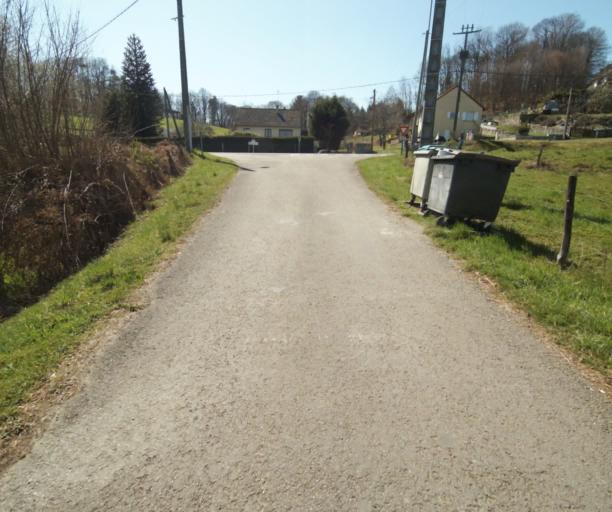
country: FR
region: Limousin
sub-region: Departement de la Correze
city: Saint-Mexant
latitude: 45.2763
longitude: 1.6644
